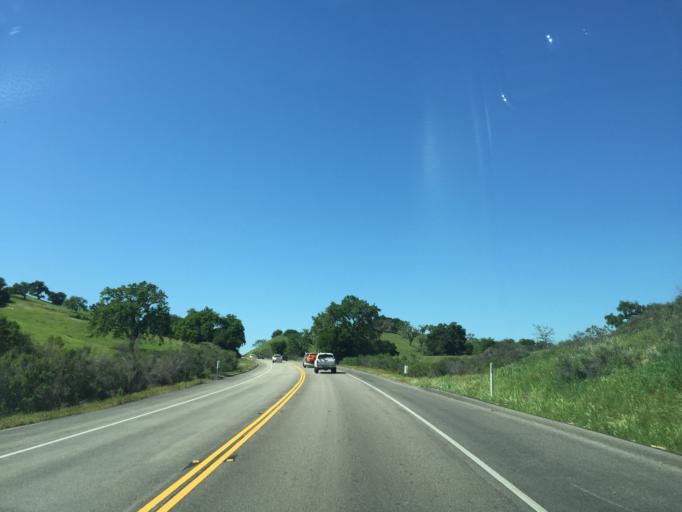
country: US
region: California
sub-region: Santa Barbara County
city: Los Olivos
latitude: 34.6748
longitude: -120.1305
